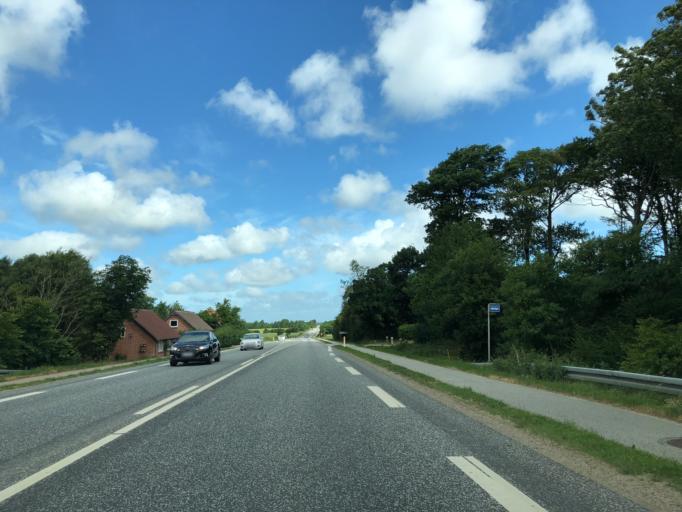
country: DK
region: Central Jutland
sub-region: Struer Kommune
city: Struer
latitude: 56.4283
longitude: 8.5987
